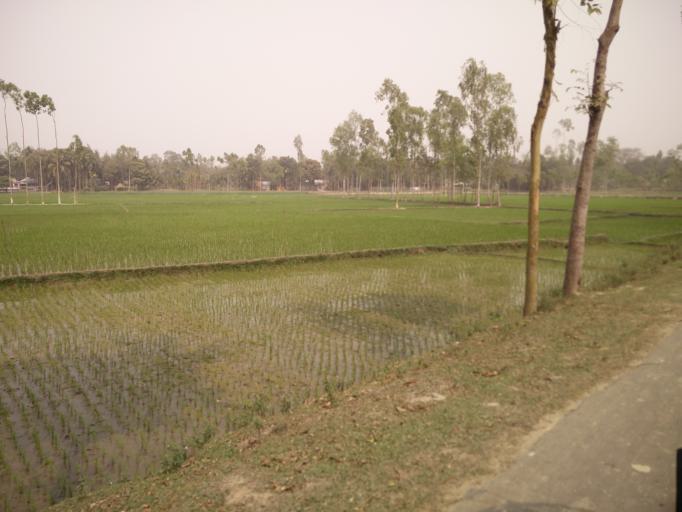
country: BD
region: Rangpur Division
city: Nageswari
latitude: 25.8823
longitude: 89.6961
